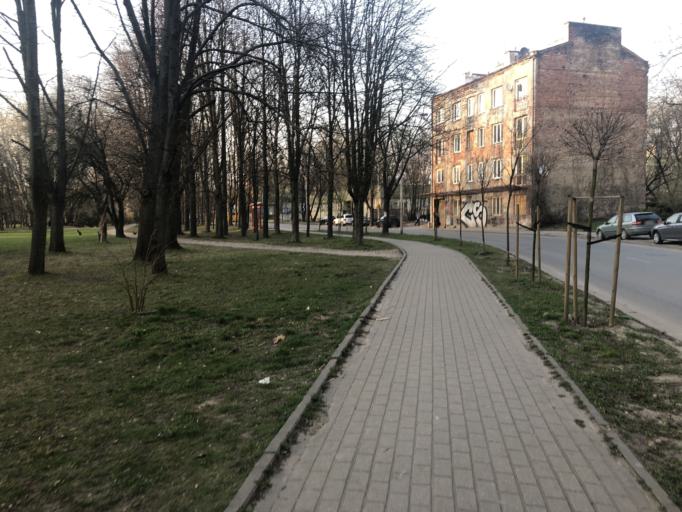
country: PL
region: Masovian Voivodeship
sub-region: Warszawa
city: Ochota
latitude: 52.2243
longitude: 20.9691
